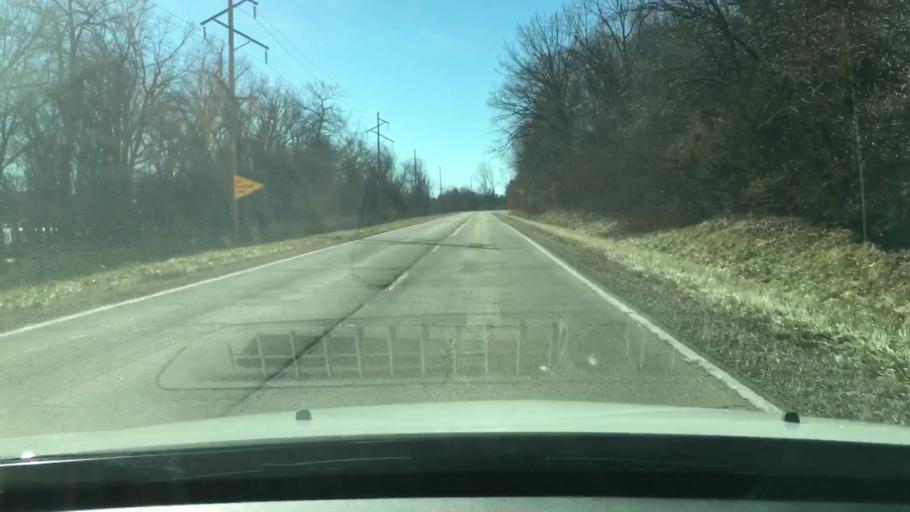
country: US
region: Illinois
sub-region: Fulton County
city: Astoria
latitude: 40.1896
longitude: -90.2085
